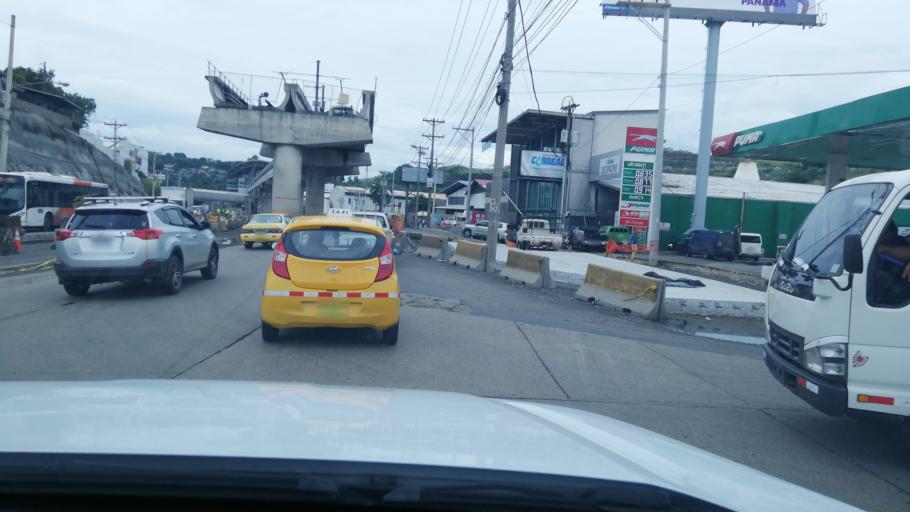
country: PA
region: Panama
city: Las Cumbres
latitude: 9.0663
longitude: -79.5171
